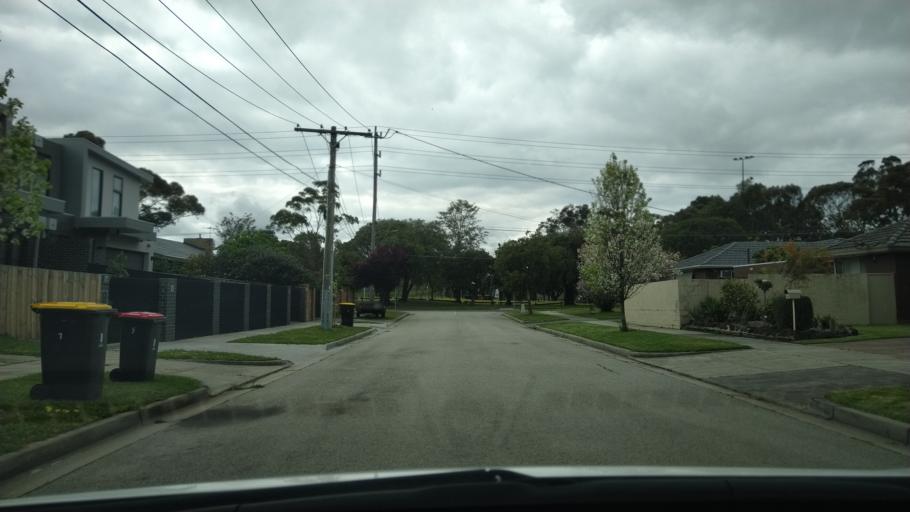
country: AU
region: Victoria
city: Highett
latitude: -37.9603
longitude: 145.0701
